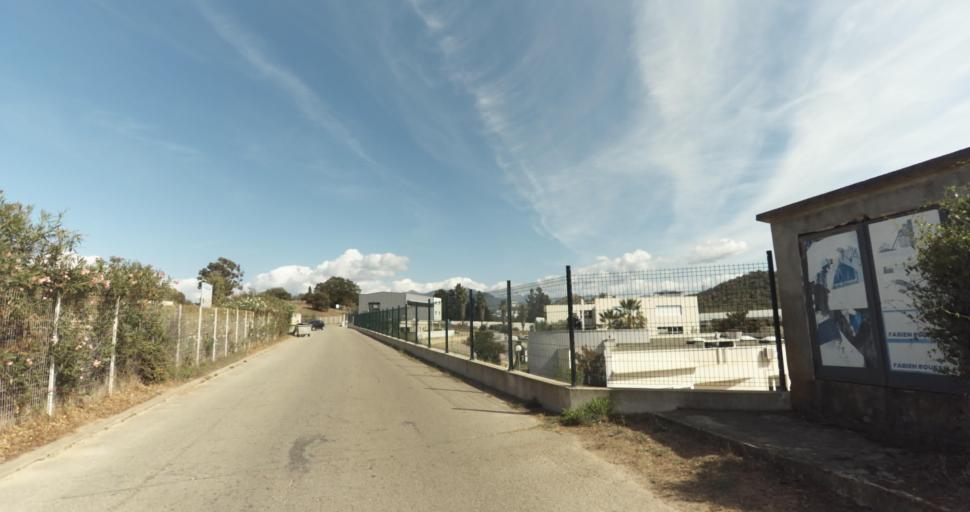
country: FR
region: Corsica
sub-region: Departement de la Corse-du-Sud
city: Ajaccio
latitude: 41.9484
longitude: 8.7556
